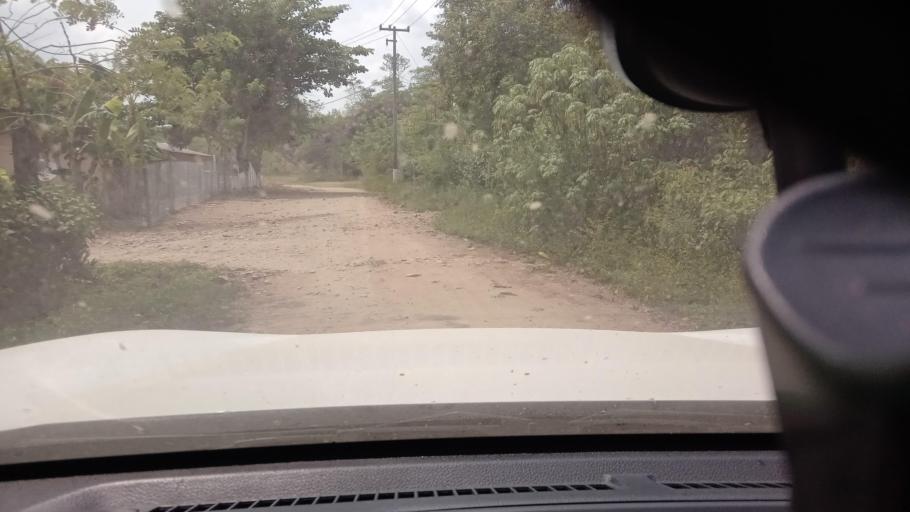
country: MX
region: Chiapas
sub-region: Tecpatan
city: Raudales Malpaso
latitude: 17.3011
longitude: -93.8610
